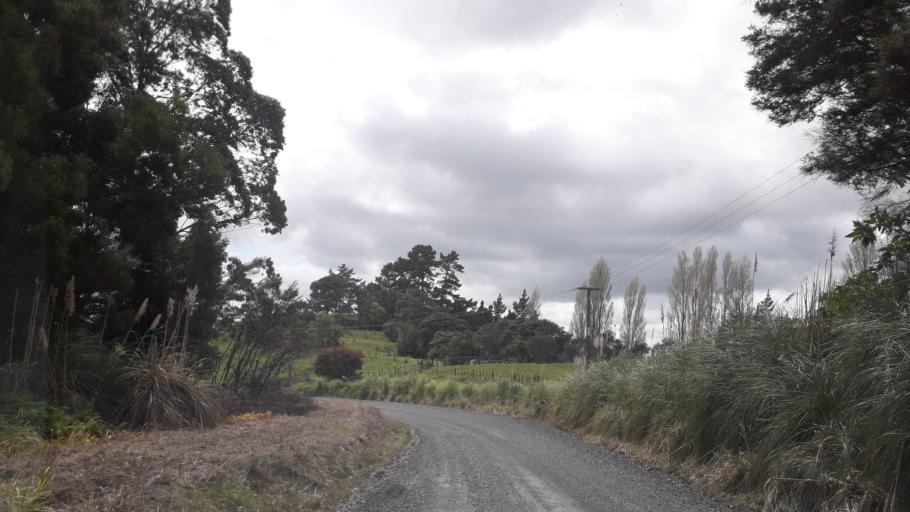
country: NZ
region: Northland
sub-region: Far North District
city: Kaitaia
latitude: -35.1557
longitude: 173.3460
